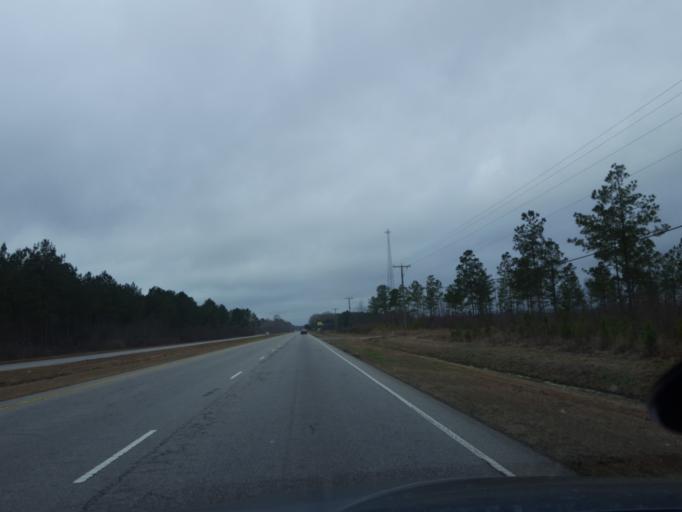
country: US
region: North Carolina
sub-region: Washington County
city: Plymouth
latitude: 35.8118
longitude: -76.8548
